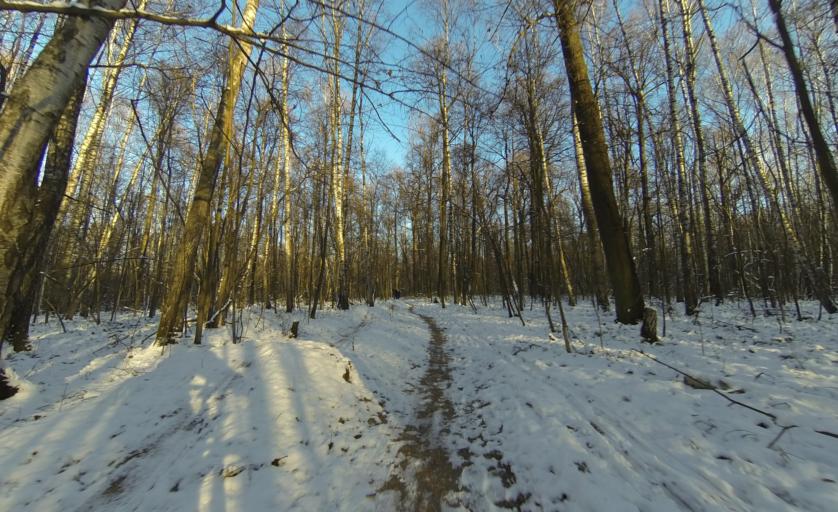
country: RU
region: Moskovskaya
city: Bogorodskoye
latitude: 55.8352
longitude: 37.6997
